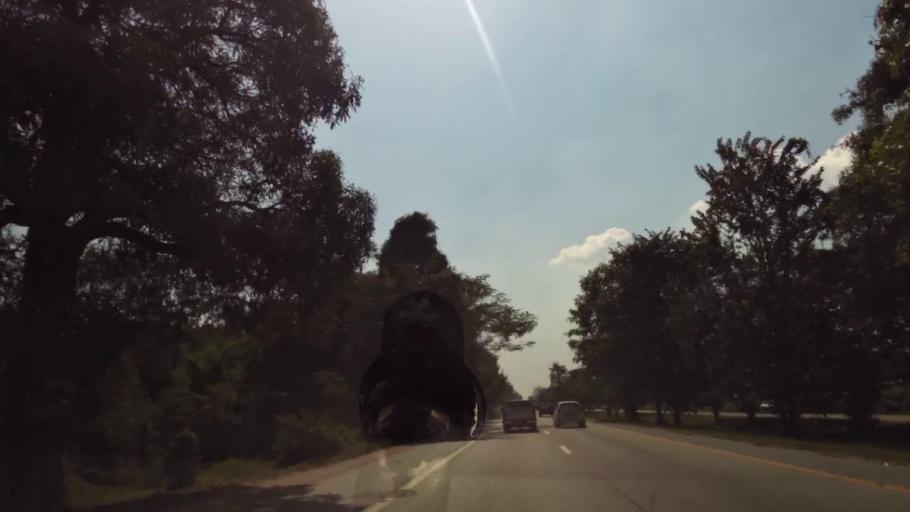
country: TH
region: Phichit
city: Wachira Barami
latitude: 16.5573
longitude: 100.1477
